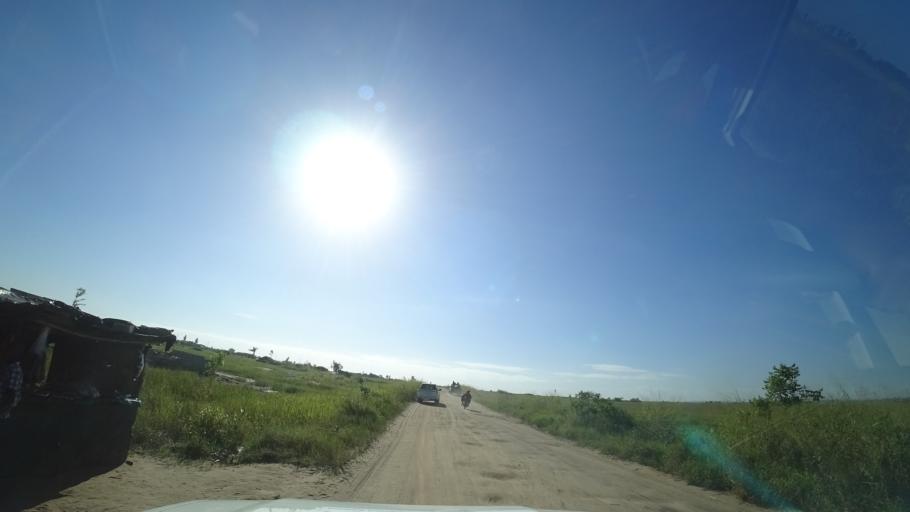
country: MZ
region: Sofala
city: Beira
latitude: -19.7633
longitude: 34.9036
